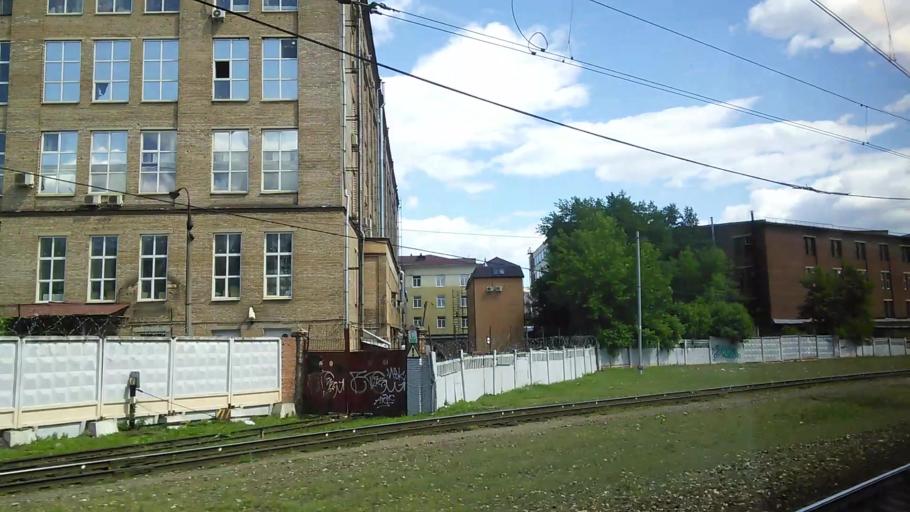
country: RU
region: Moscow
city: Mar'ina Roshcha
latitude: 55.8084
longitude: 37.5853
